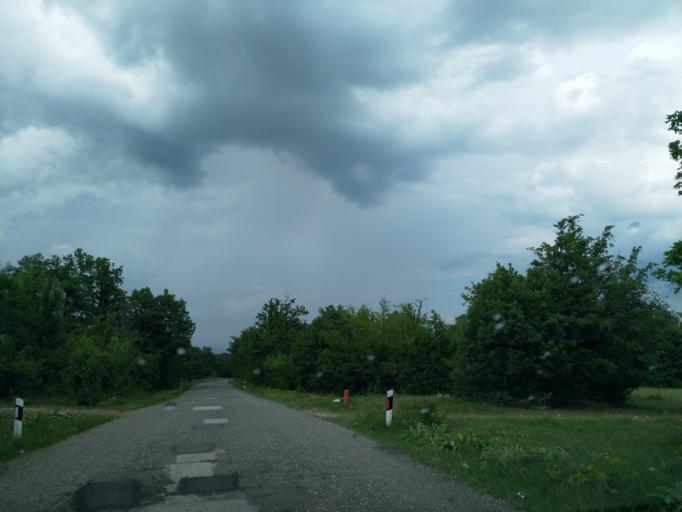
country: RS
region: Central Serbia
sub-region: Zajecarski Okrug
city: Boljevac
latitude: 43.9650
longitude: 21.9656
